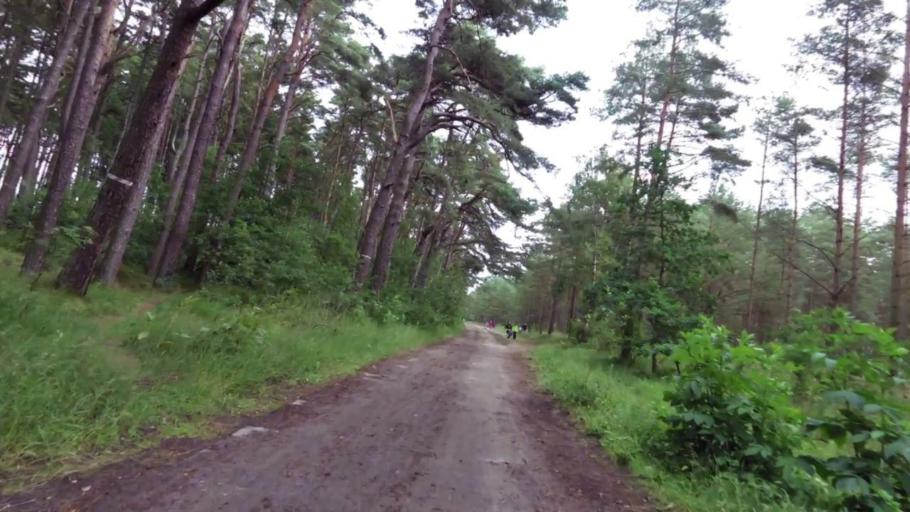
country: PL
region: West Pomeranian Voivodeship
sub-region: Powiat slawienski
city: Darlowo
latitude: 54.5029
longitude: 16.4593
